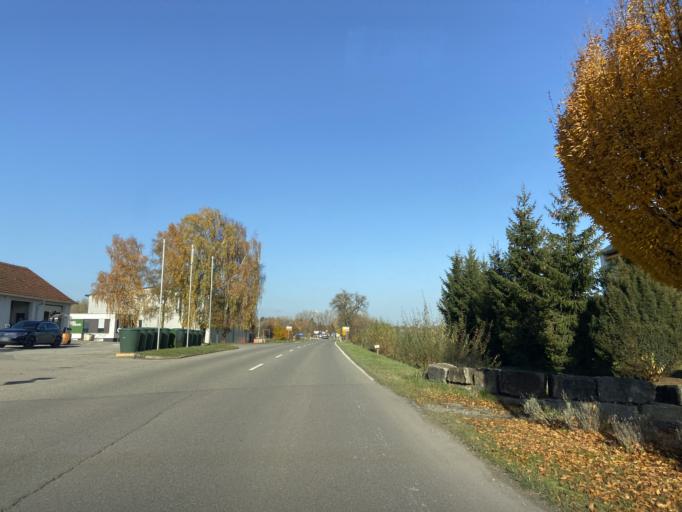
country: DE
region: Baden-Wuerttemberg
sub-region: Tuebingen Region
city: Ennetach
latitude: 48.0300
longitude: 9.2979
